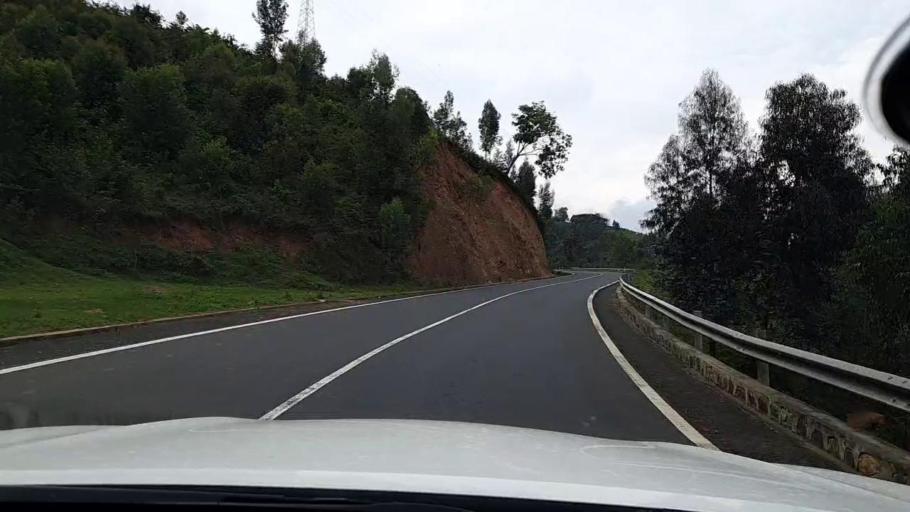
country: RW
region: Western Province
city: Kibuye
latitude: -2.1711
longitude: 29.2903
